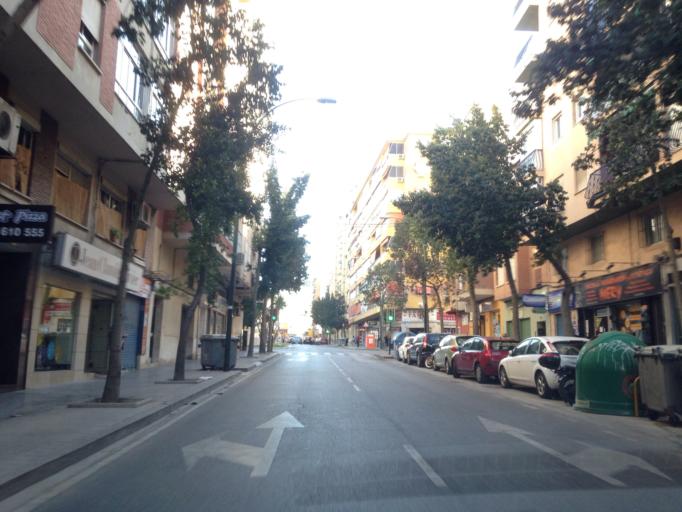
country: ES
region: Andalusia
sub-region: Provincia de Malaga
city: Malaga
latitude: 36.7315
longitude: -4.4180
